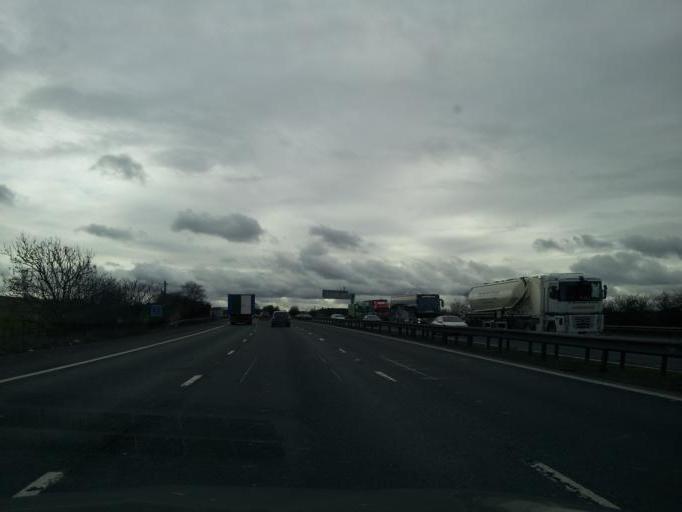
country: GB
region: England
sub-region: Staffordshire
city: Audley
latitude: 53.0350
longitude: -2.3291
